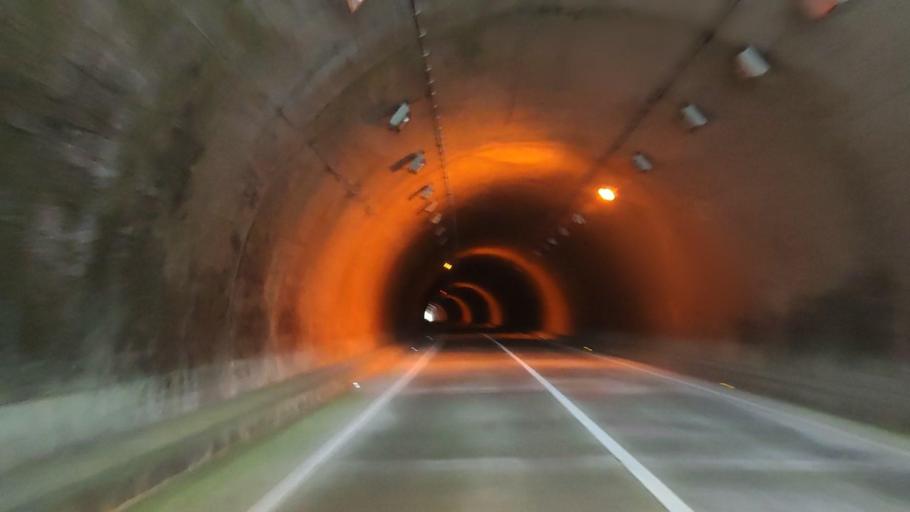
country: JP
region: Shizuoka
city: Heda
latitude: 34.9081
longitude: 138.8476
